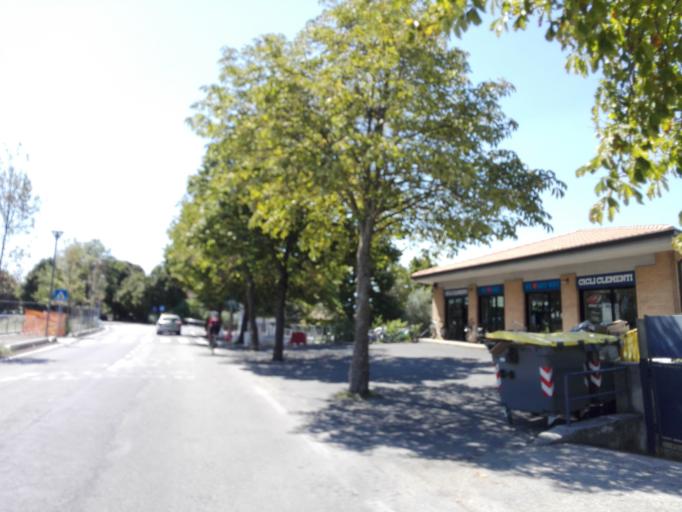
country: IT
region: Umbria
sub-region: Provincia di Perugia
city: Foligno
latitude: 42.9551
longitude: 12.6945
